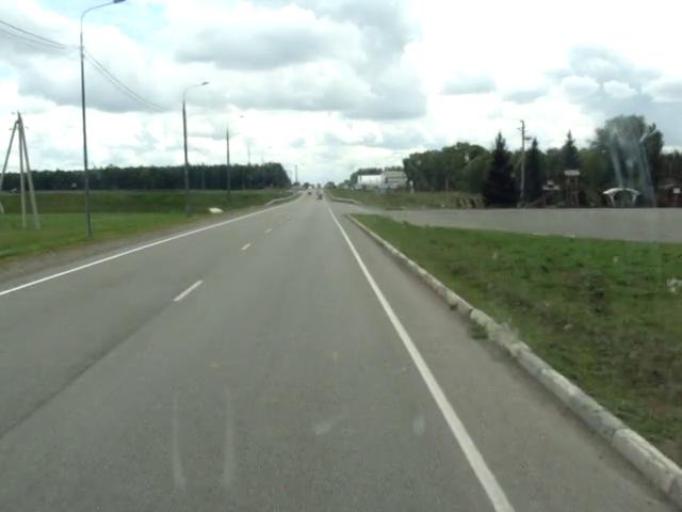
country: RU
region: Altai Krai
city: Zarya
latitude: 52.5793
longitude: 85.1768
